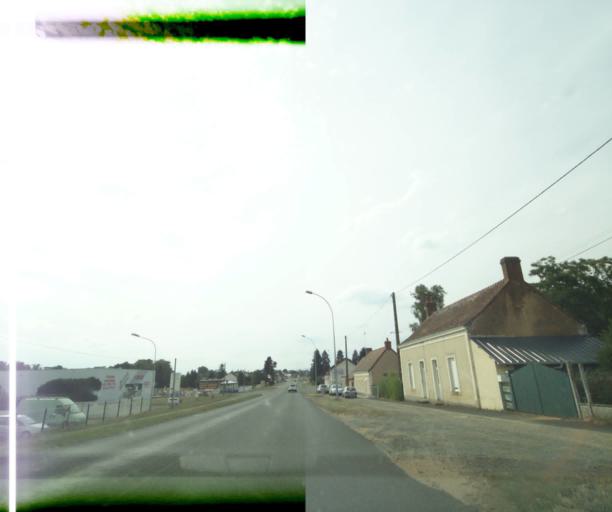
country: FR
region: Pays de la Loire
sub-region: Departement de la Sarthe
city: Ecommoy
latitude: 47.8244
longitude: 0.2881
